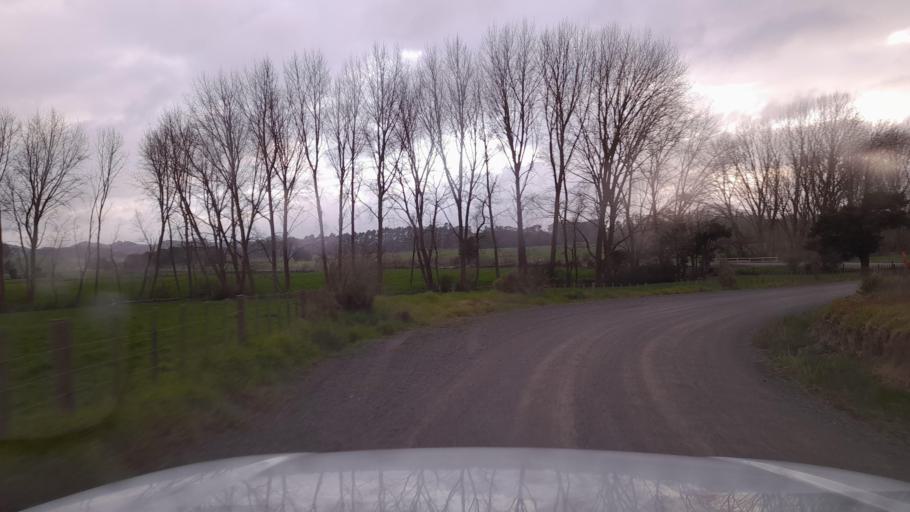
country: NZ
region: Northland
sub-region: Whangarei
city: Maungatapere
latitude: -35.6299
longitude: 174.1957
